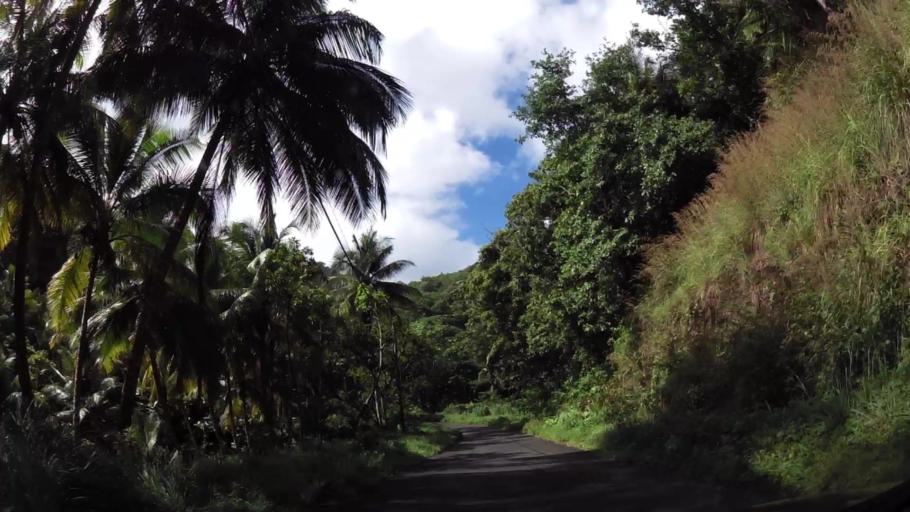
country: DM
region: Saint David
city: Castle Bruce
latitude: 15.4845
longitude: -61.2563
